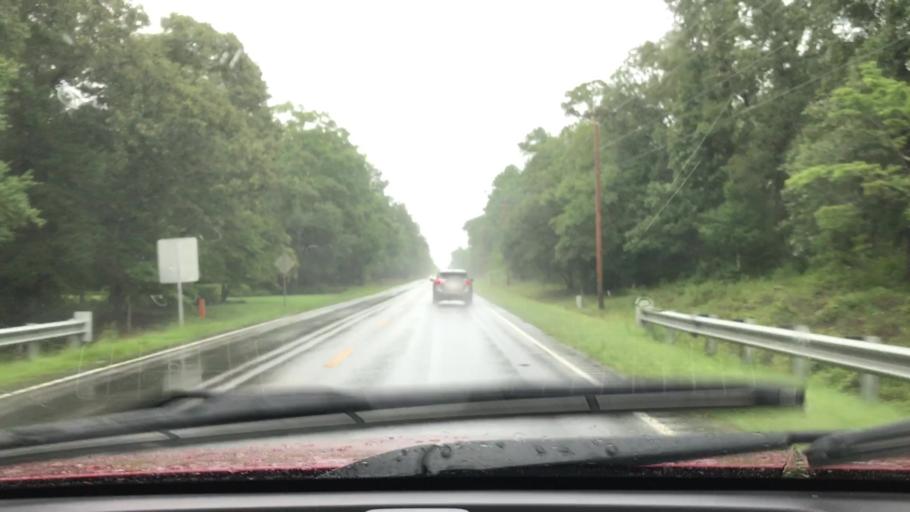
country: US
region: South Carolina
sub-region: Horry County
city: Conway
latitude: 33.7509
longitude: -79.0776
